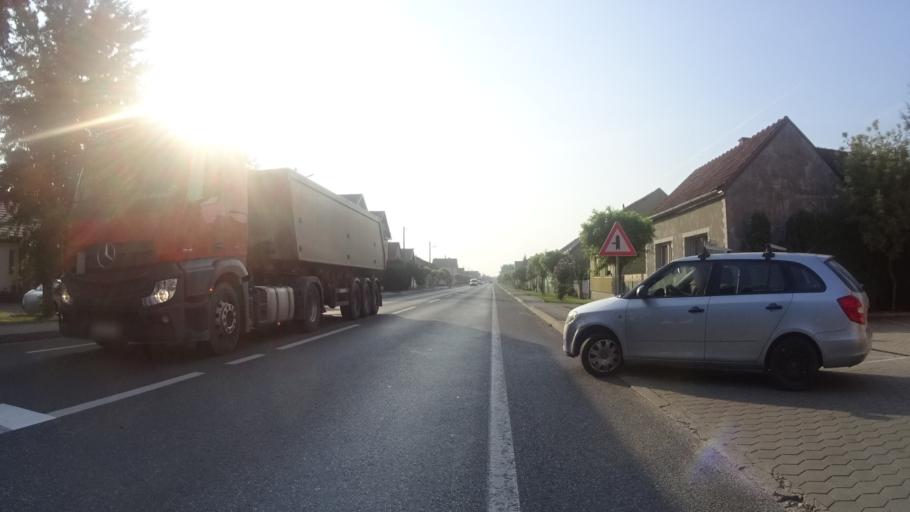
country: HR
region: Varazdinska
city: Sracinec
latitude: 46.3280
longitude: 16.2835
